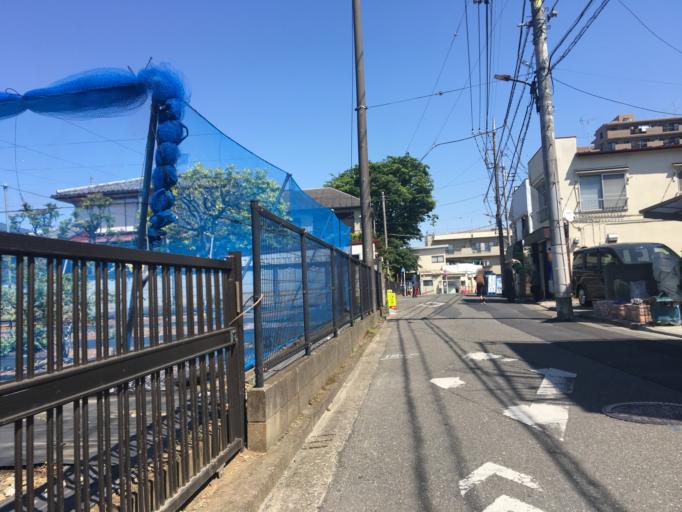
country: JP
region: Tokyo
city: Higashimurayama-shi
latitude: 35.7336
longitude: 139.4864
